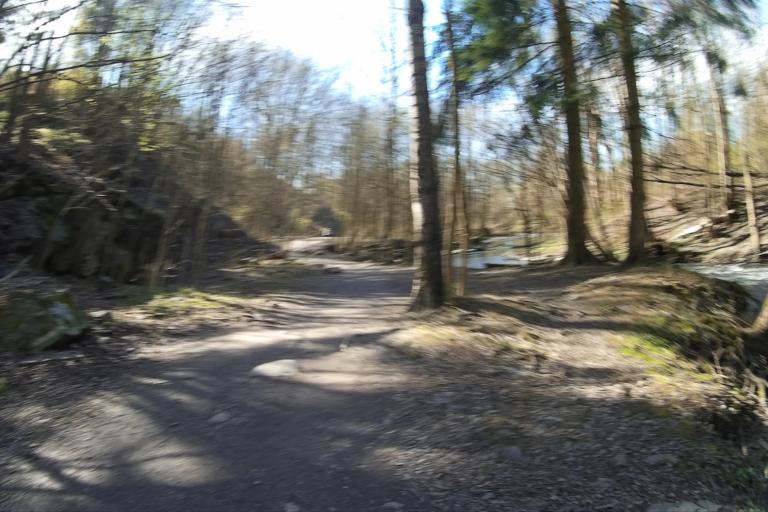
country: NO
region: Oslo
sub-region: Oslo
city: Oslo
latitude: 59.9035
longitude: 10.7978
